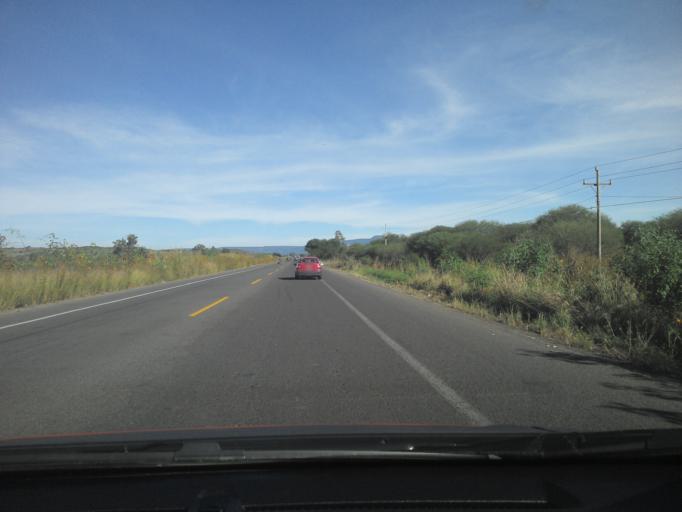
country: MX
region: Jalisco
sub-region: Teuchitlan
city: La Estanzuela
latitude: 20.6714
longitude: -103.8141
